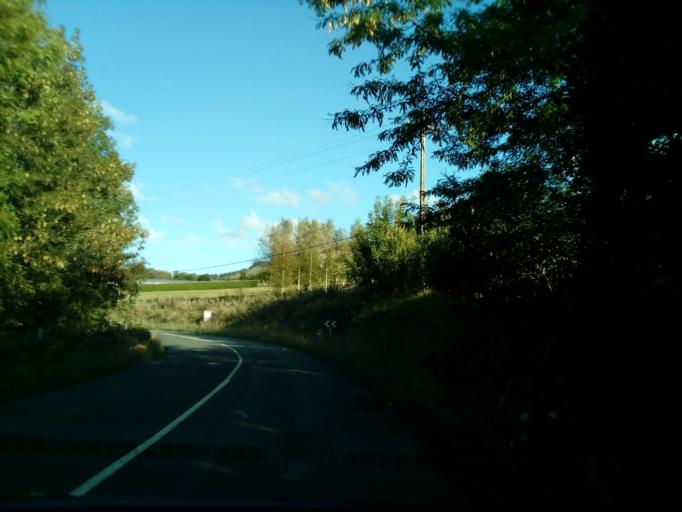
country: ES
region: Basque Country
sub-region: Provincia de Guipuzcoa
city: Urnieta
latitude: 43.2314
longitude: -1.9929
